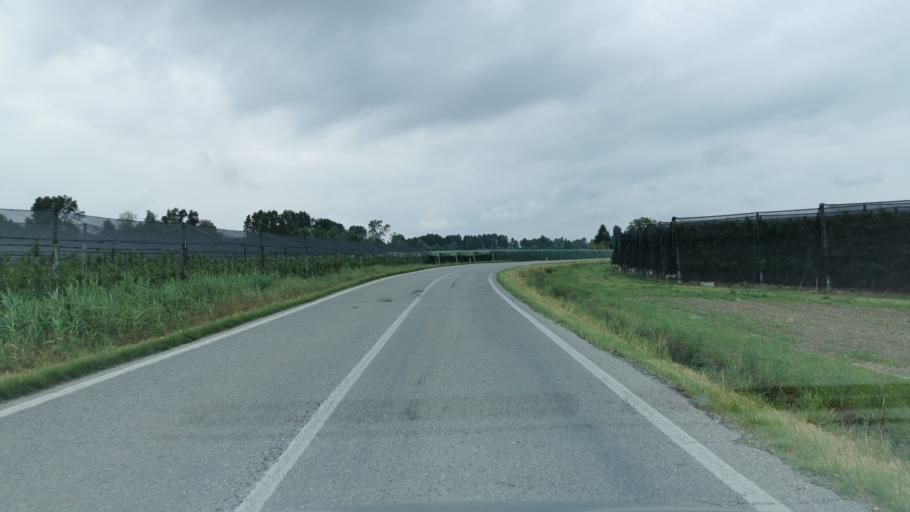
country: IT
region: Piedmont
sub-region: Provincia di Cuneo
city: Savigliano
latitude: 44.6177
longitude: 7.6294
